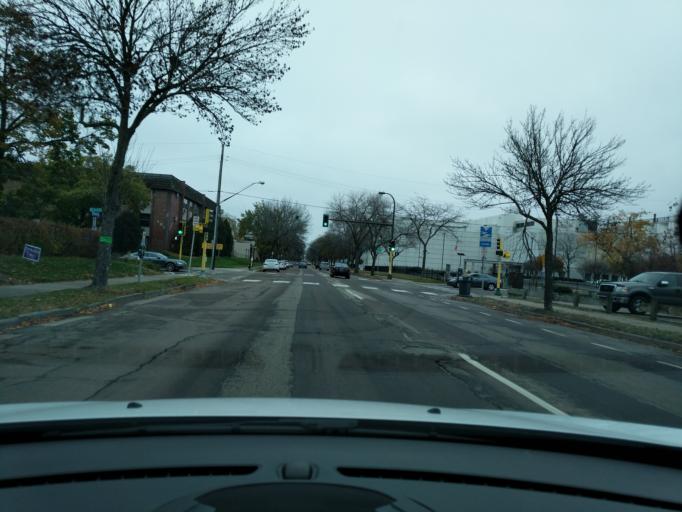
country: US
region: Minnesota
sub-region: Hennepin County
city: Minneapolis
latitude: 44.9860
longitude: -93.2528
